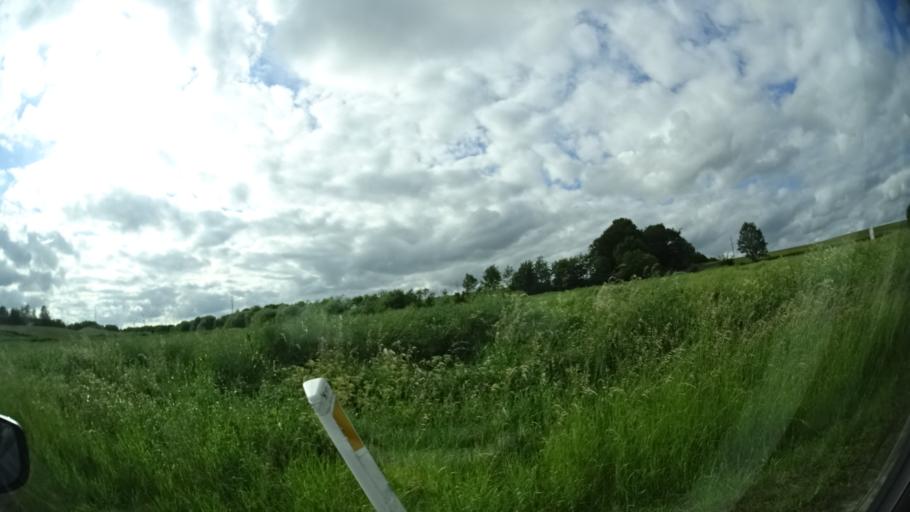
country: DK
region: Central Jutland
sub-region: Syddjurs Kommune
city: Ronde
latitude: 56.3140
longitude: 10.4187
